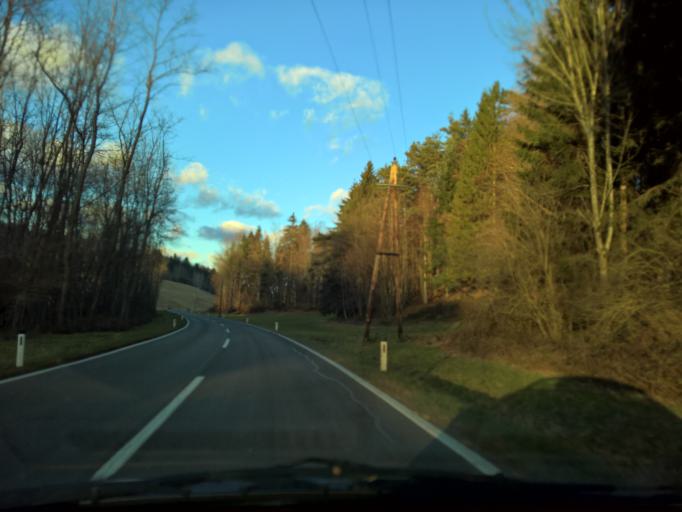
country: AT
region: Styria
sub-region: Politischer Bezirk Leibnitz
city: Sulztal an der Weinstrasse
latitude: 46.7045
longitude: 15.5040
